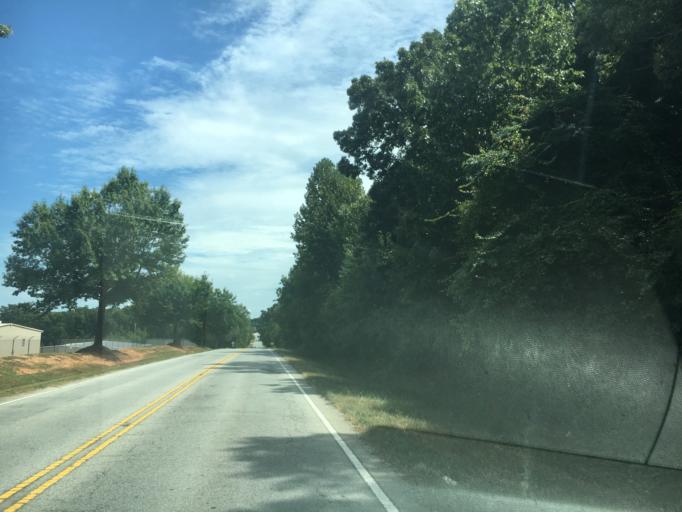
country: US
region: South Carolina
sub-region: Laurens County
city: Laurens
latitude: 34.5303
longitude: -82.0511
